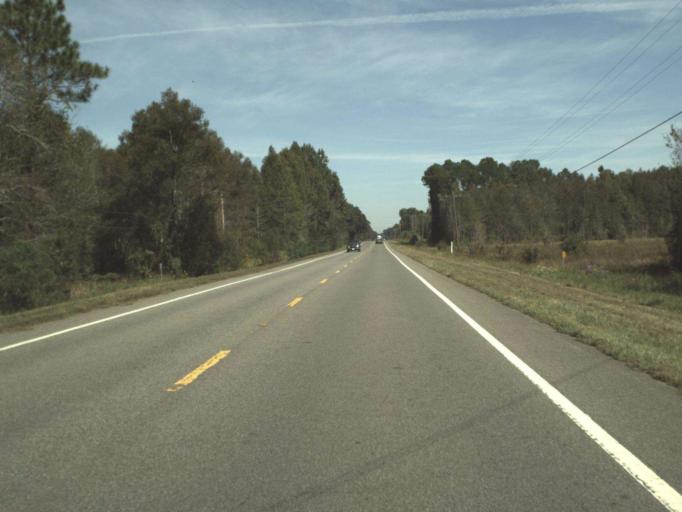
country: US
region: Florida
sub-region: Washington County
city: Chipley
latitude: 30.6818
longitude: -85.5697
